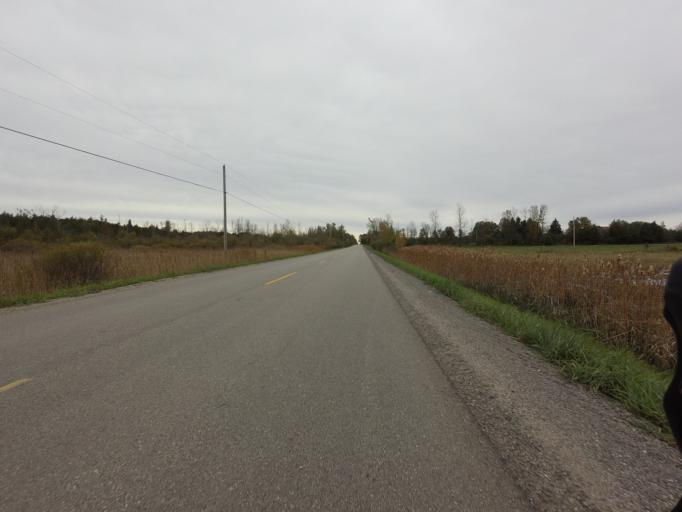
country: CA
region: Ontario
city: Brockville
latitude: 44.7566
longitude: -75.7744
